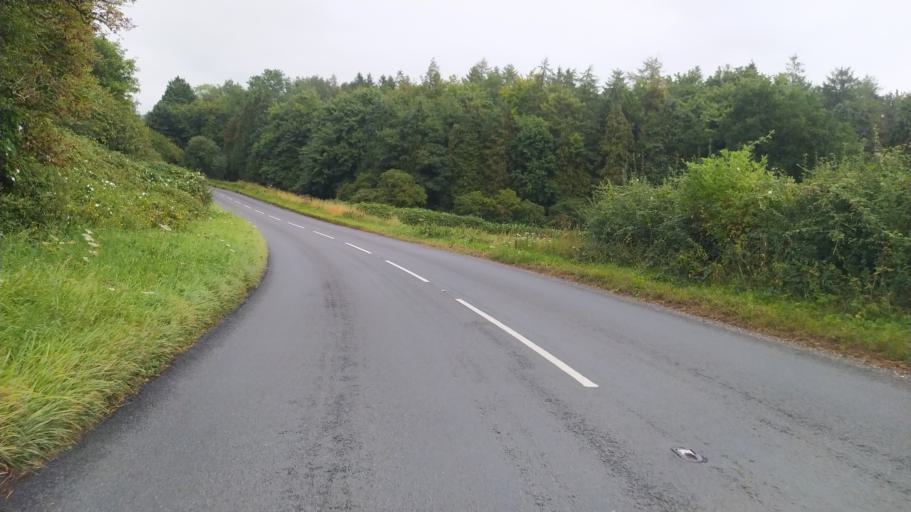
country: GB
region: England
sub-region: Wiltshire
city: Ansty
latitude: 51.0381
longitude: -2.0435
